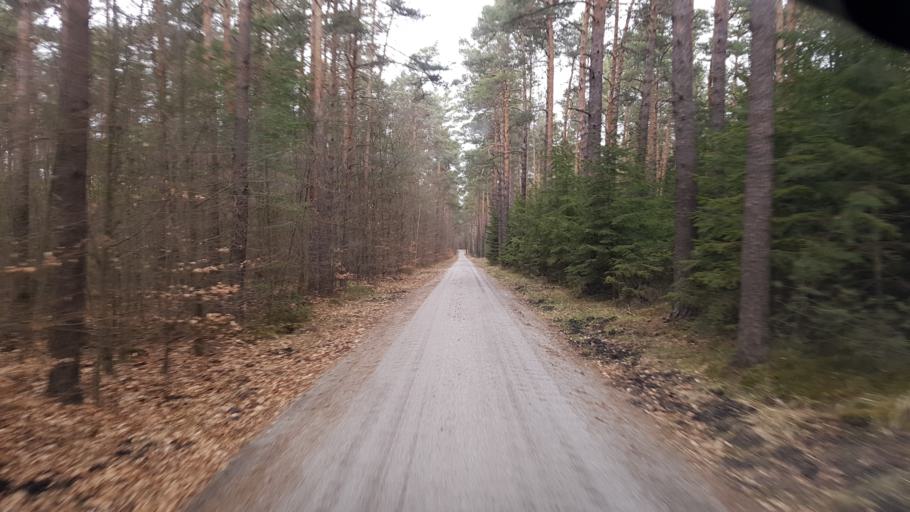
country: DE
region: Brandenburg
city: Finsterwalde
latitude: 51.5726
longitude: 13.7043
